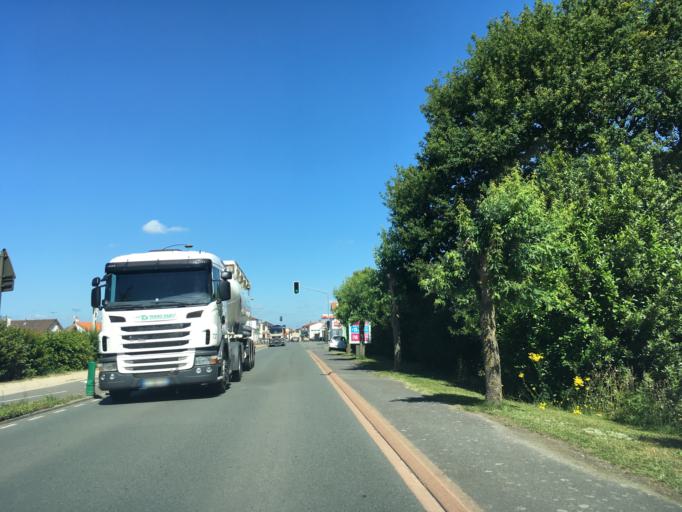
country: FR
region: Pays de la Loire
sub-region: Departement de la Vendee
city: Saint-Georges-de-Montaigu
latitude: 46.9443
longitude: -1.2894
